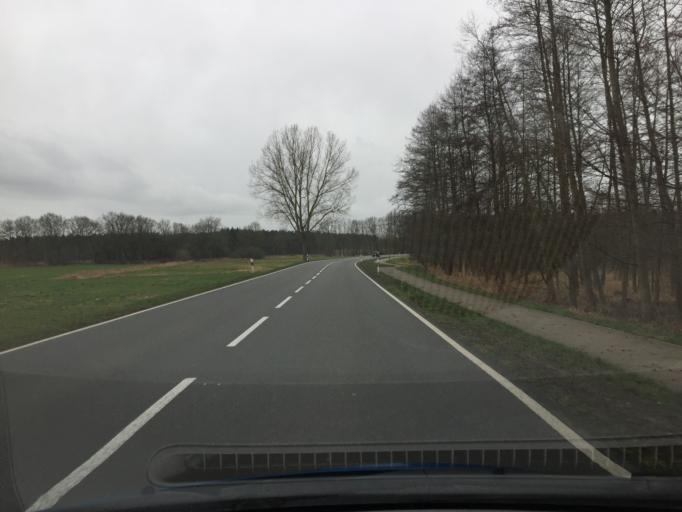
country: DE
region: Lower Saxony
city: Rosche
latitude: 53.0130
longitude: 10.7301
